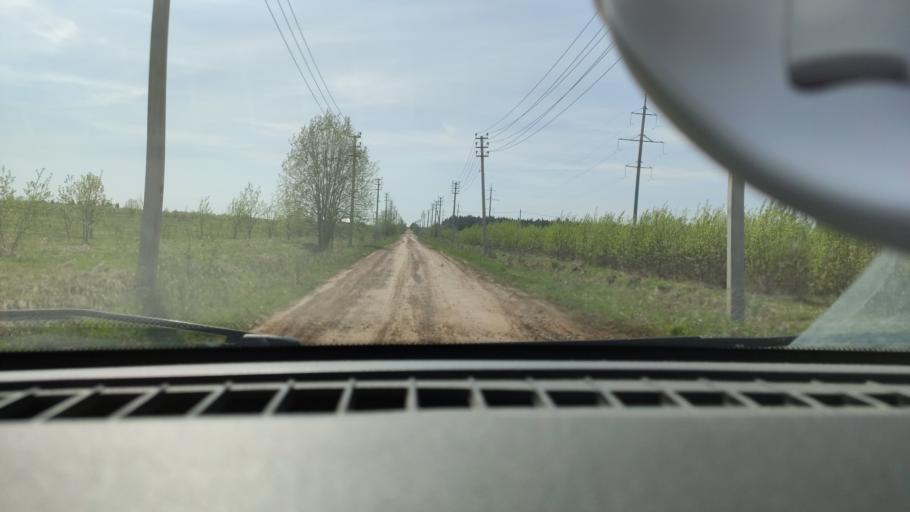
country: RU
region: Perm
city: Kultayevo
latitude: 57.8910
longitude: 55.8653
